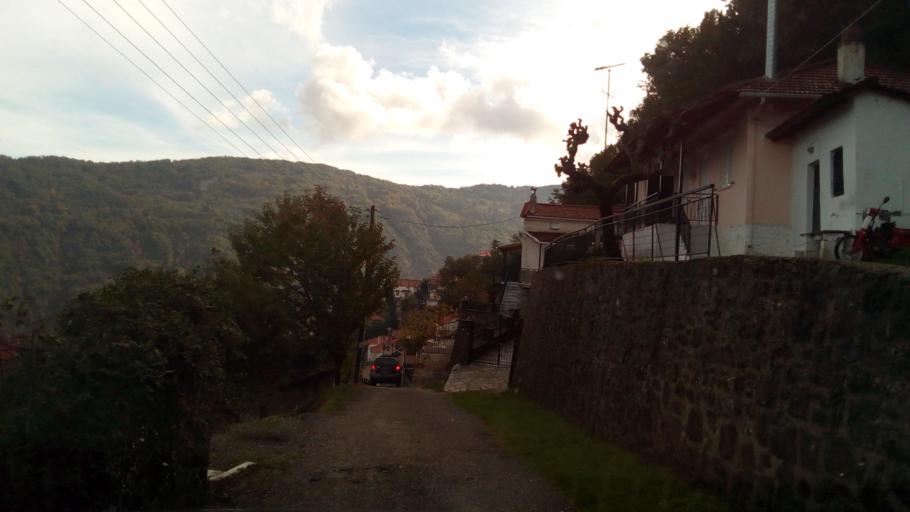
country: GR
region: Central Greece
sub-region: Nomos Fokidos
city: Lidoriki
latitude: 38.4896
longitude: 22.0524
